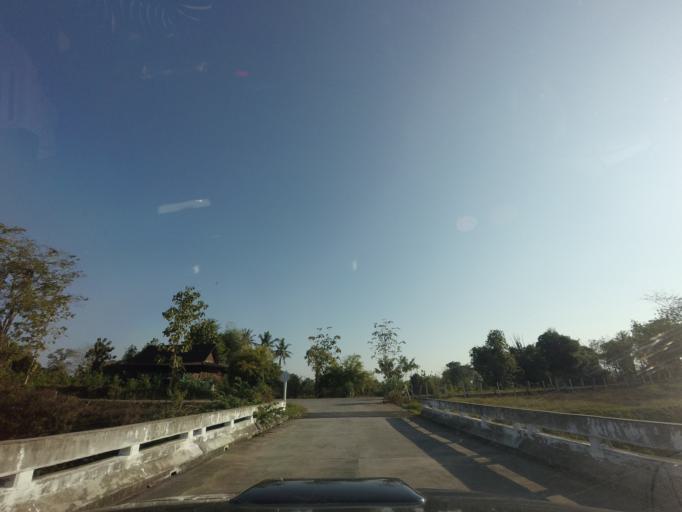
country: TH
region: Chiang Mai
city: San Sai
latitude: 18.9021
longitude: 99.1209
